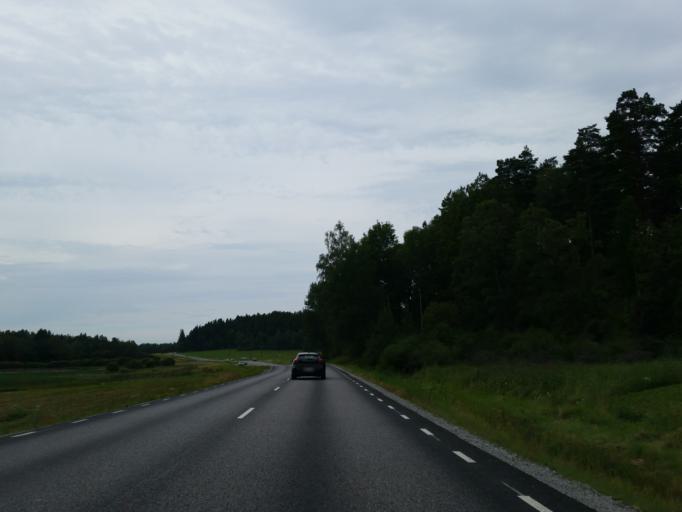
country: SE
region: Stockholm
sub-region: Salems Kommun
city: Ronninge
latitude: 59.2245
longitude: 17.7367
